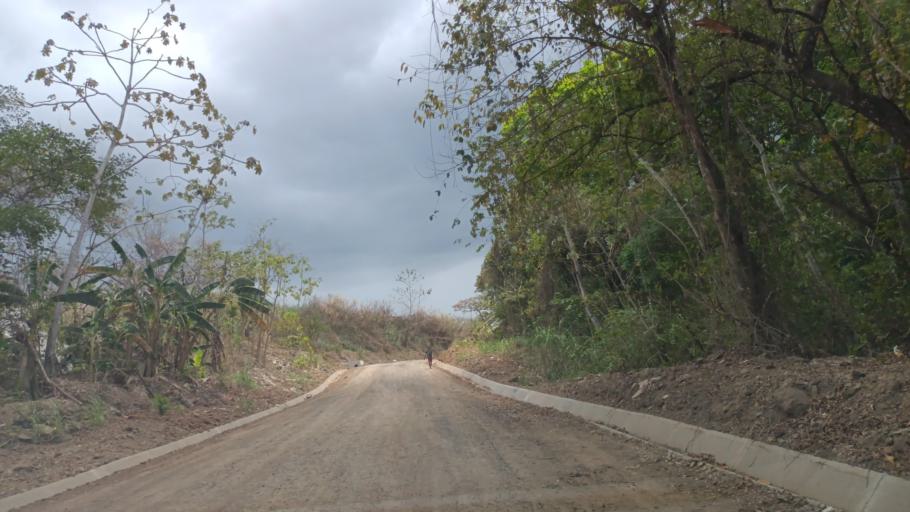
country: PA
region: Panama
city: Las Cumbres
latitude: 9.0675
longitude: -79.5693
